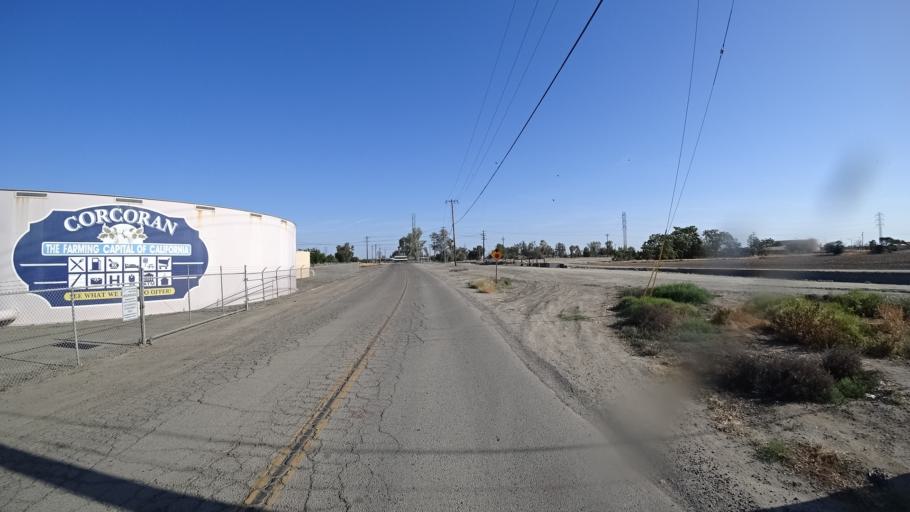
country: US
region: California
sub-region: Kings County
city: Corcoran
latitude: 36.1073
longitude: -119.5543
